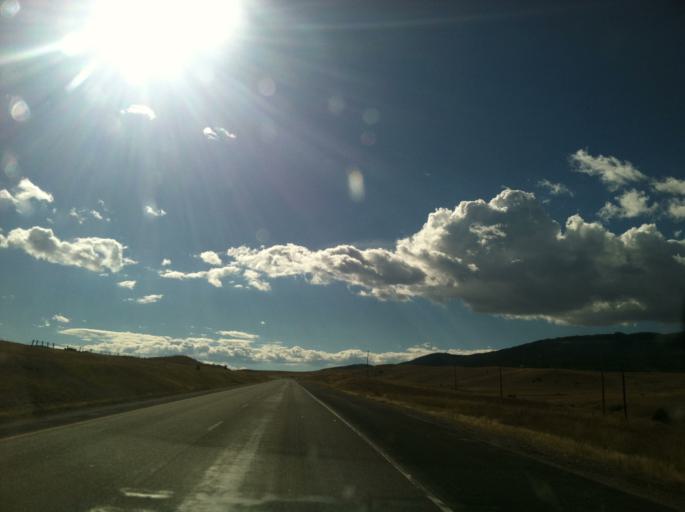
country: US
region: Montana
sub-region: Jefferson County
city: Whitehall
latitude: 45.8952
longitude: -111.8408
